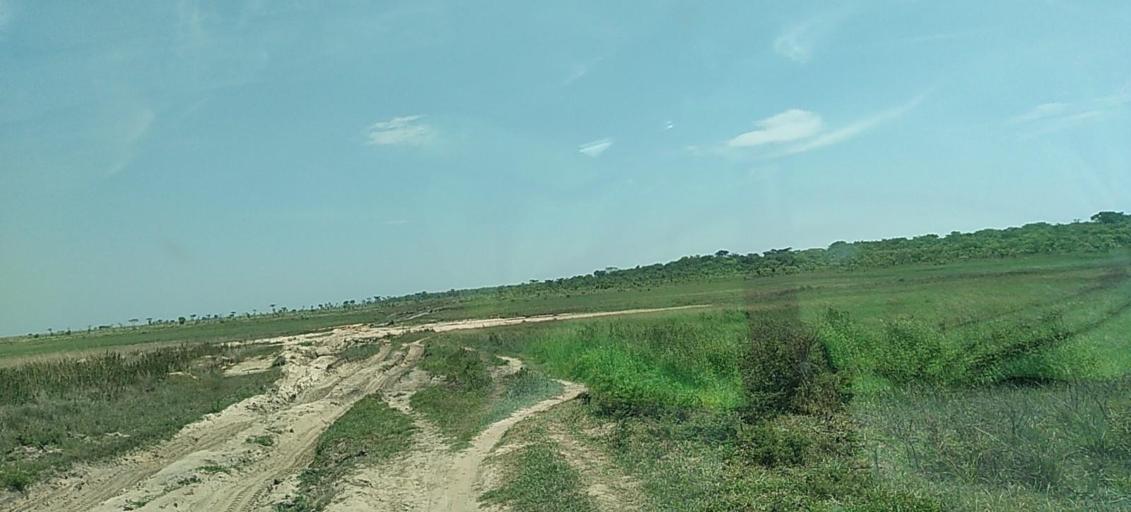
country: ZM
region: North-Western
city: Mwinilunga
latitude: -11.6679
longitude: 25.2047
